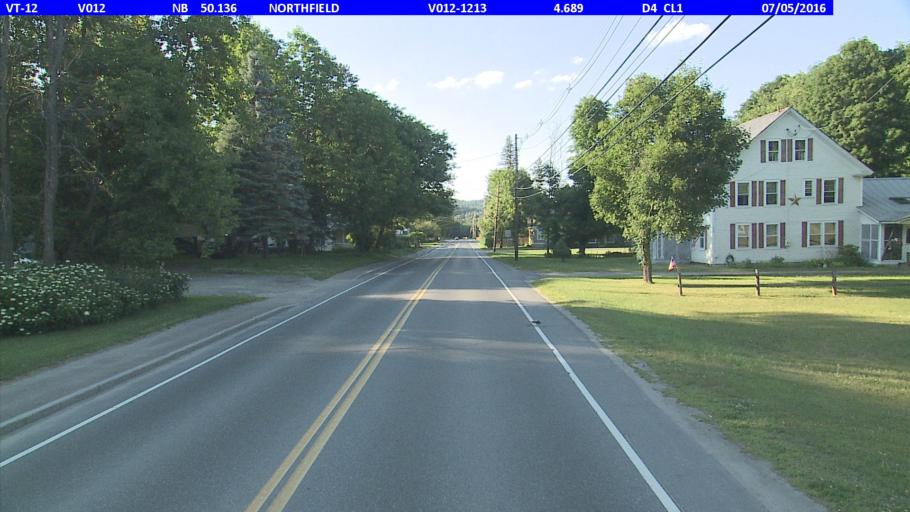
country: US
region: Vermont
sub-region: Washington County
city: Northfield
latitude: 44.1558
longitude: -72.6569
